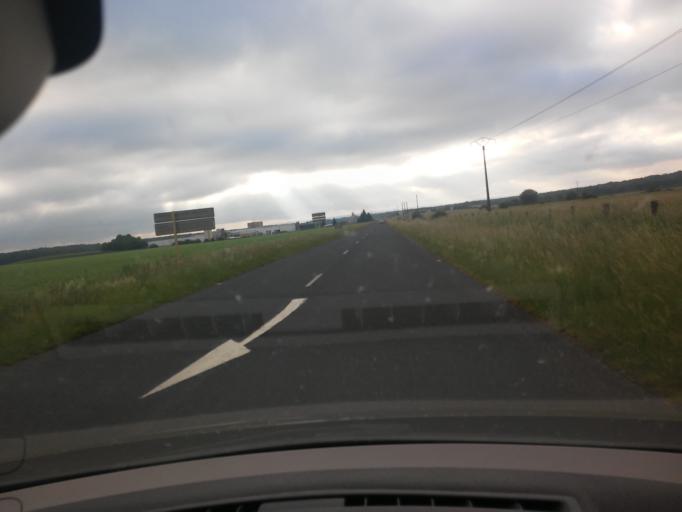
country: FR
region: Lorraine
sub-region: Departement de la Meuse
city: Vigneulles-les-Hattonchatel
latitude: 48.9787
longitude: 5.7192
